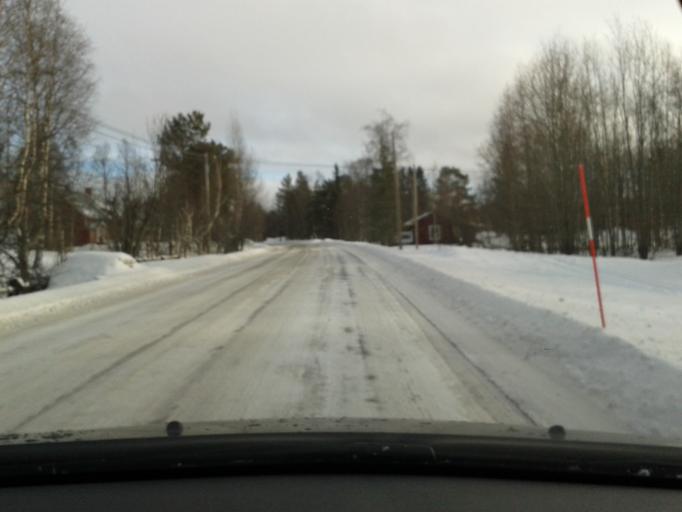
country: SE
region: Vaesterbotten
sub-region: Vilhelmina Kommun
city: Vilhelmina
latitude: 64.6323
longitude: 16.4042
